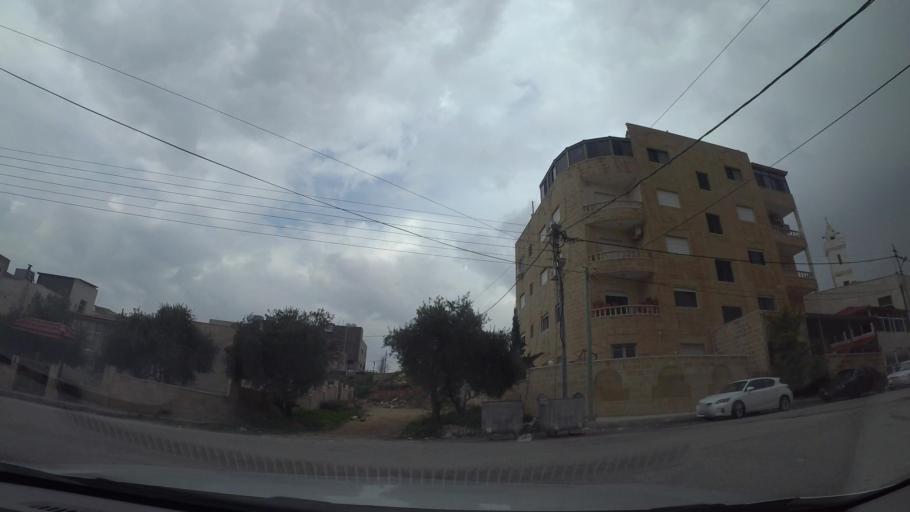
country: JO
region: Amman
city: Umm as Summaq
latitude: 31.8865
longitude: 35.8604
